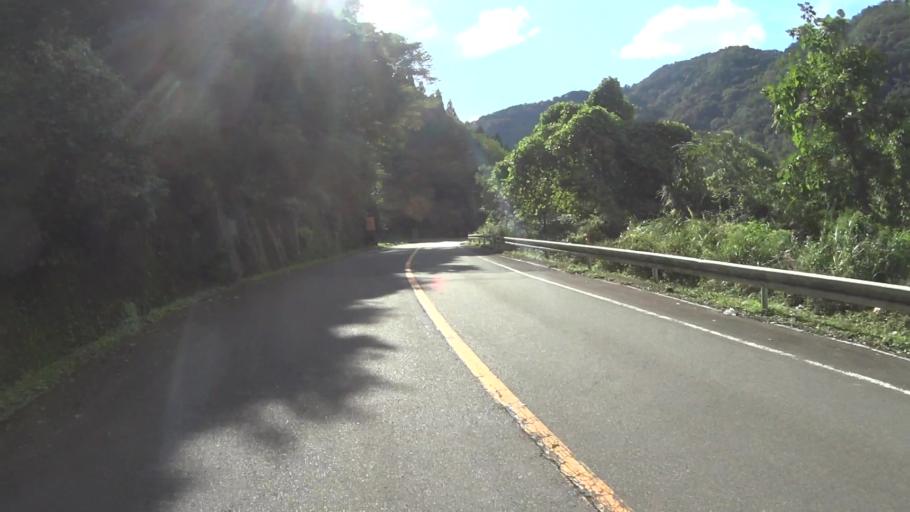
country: JP
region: Kyoto
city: Uji
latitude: 34.8911
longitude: 135.8665
